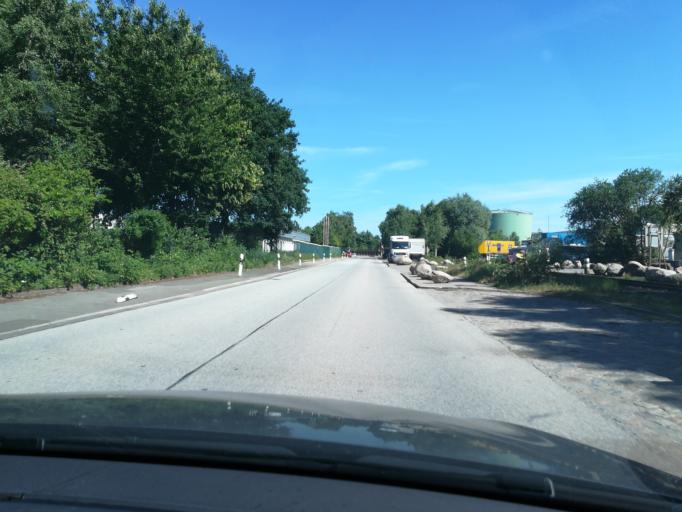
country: DE
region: Hamburg
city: Rothenburgsort
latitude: 53.5125
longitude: 10.0497
